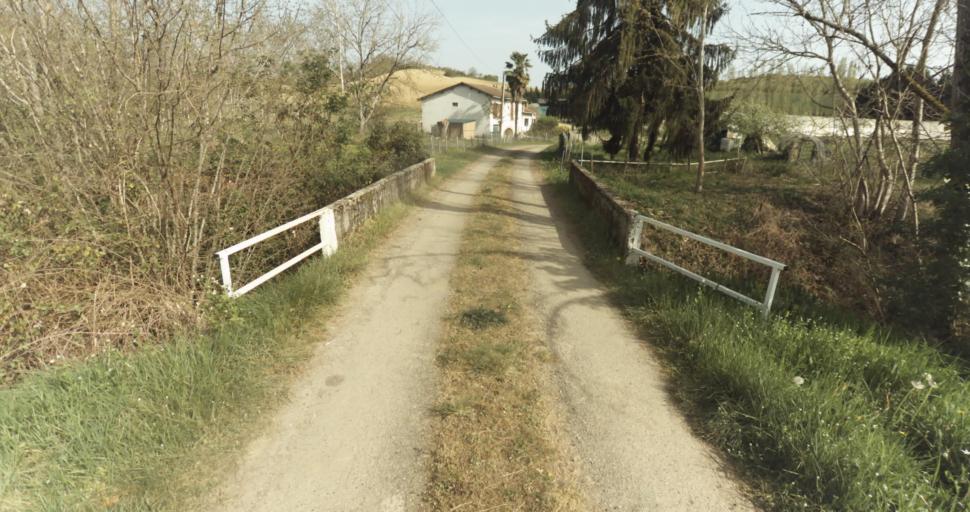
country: FR
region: Midi-Pyrenees
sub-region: Departement du Tarn-et-Garonne
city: Lafrancaise
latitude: 44.1449
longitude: 1.1788
